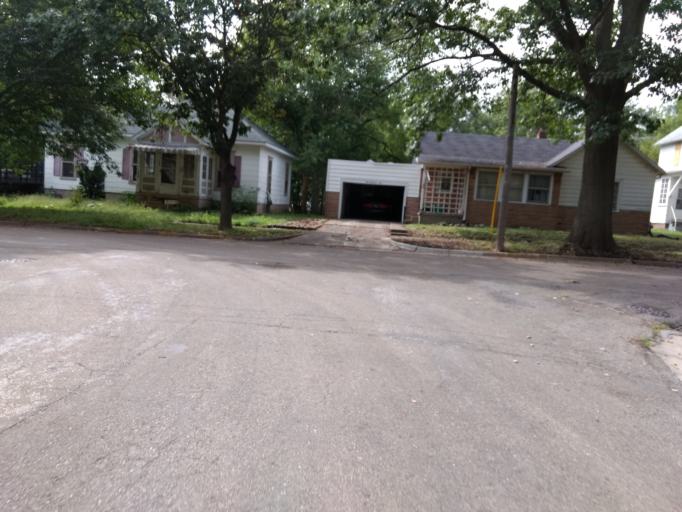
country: US
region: Illinois
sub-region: Champaign County
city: Urbana
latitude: 40.1140
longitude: -88.1977
